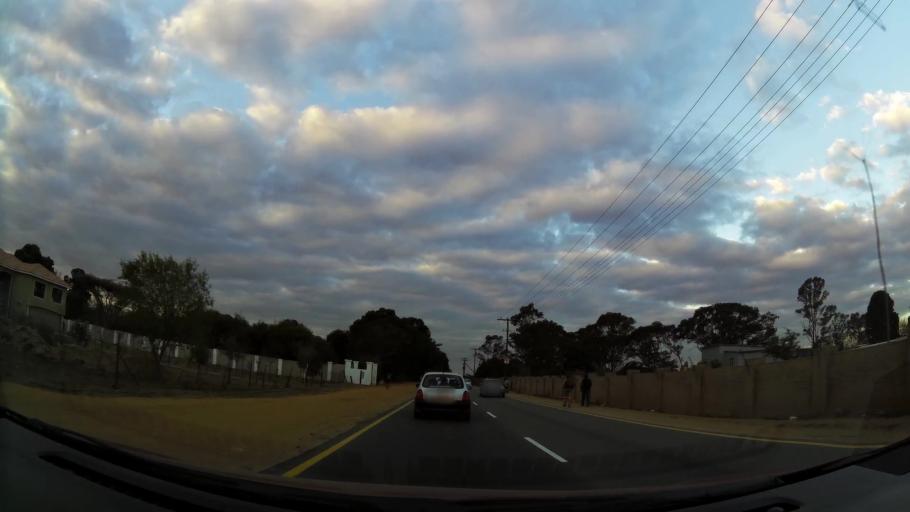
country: ZA
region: Gauteng
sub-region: City of Johannesburg Metropolitan Municipality
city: Midrand
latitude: -25.9867
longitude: 28.1562
